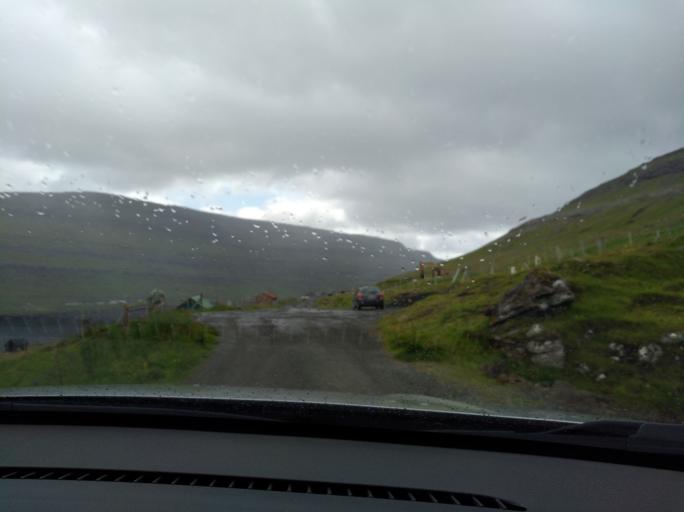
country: FO
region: Nordoyar
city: Klaksvik
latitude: 62.2203
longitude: -6.5903
